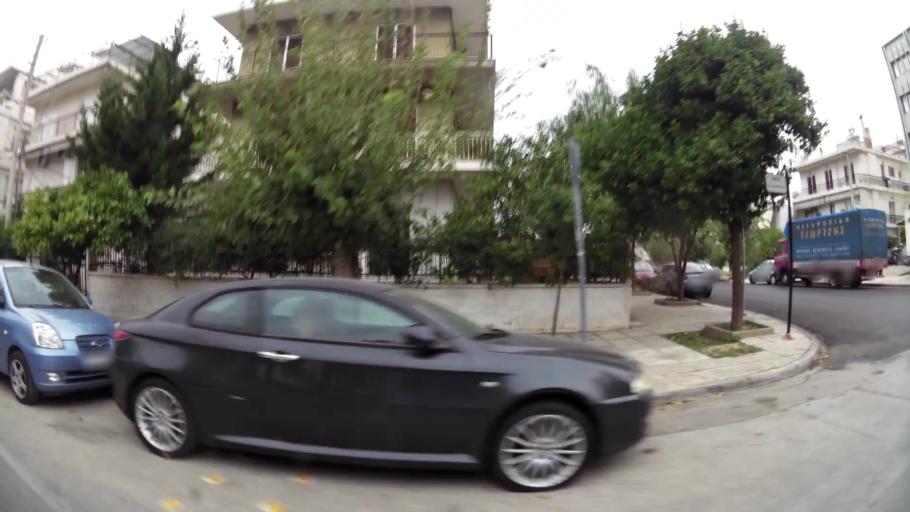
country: GR
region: Attica
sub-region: Nomarchia Athinas
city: Agios Dimitrios
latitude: 37.9238
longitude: 23.7428
